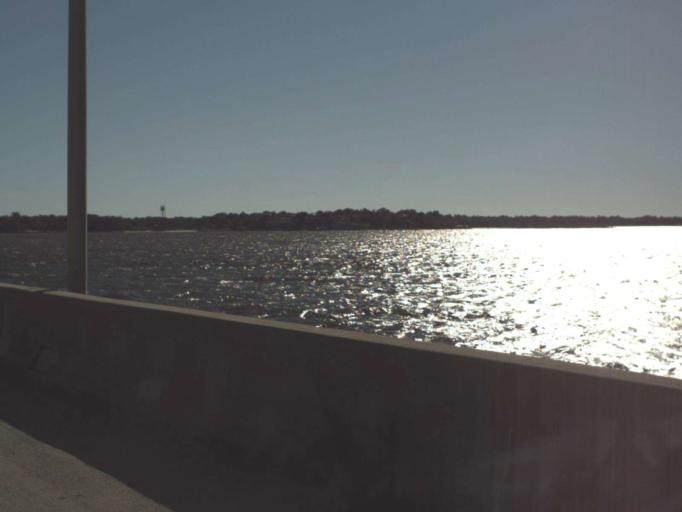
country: US
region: Florida
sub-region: Santa Rosa County
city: Gulf Breeze
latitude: 30.3786
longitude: -87.1792
